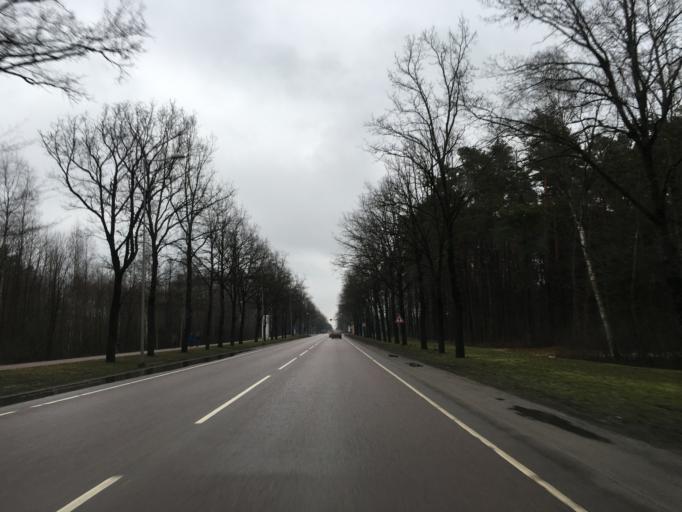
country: LV
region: Ozolnieku
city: Ozolnieki
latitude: 56.6805
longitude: 23.7792
